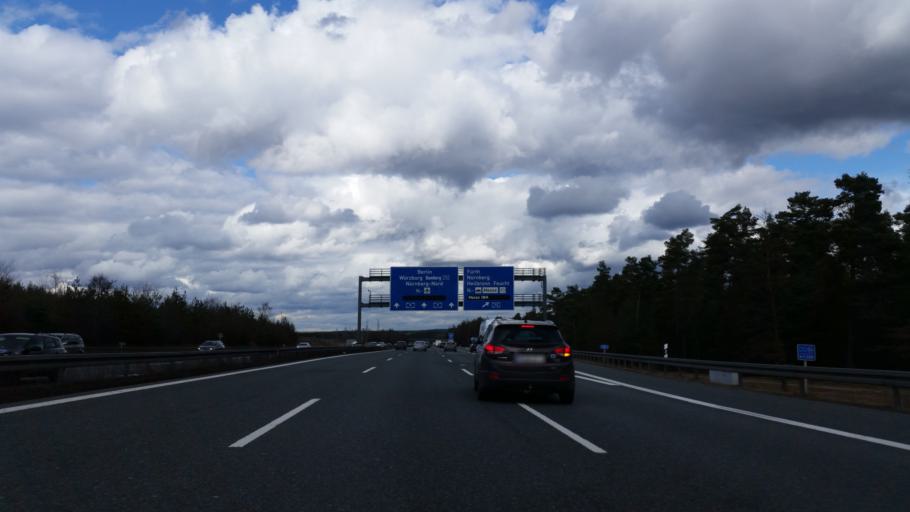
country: DE
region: Bavaria
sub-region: Regierungsbezirk Mittelfranken
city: Feucht
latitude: 49.3407
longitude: 11.2040
